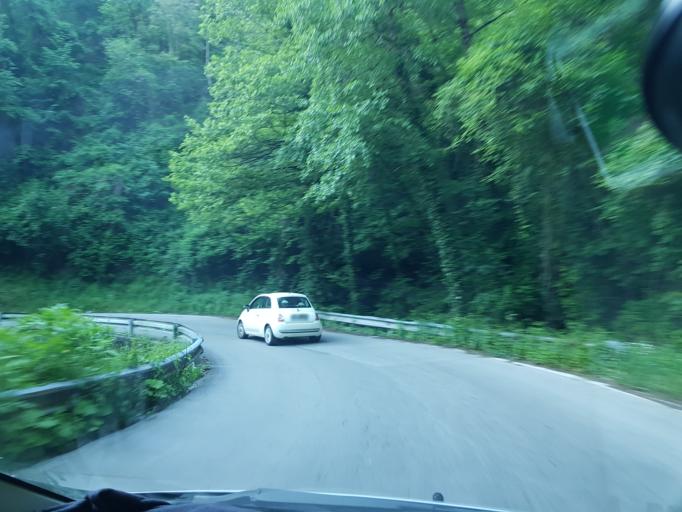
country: IT
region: Tuscany
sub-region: Provincia di Lucca
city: Minucciano
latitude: 44.1734
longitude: 10.2104
